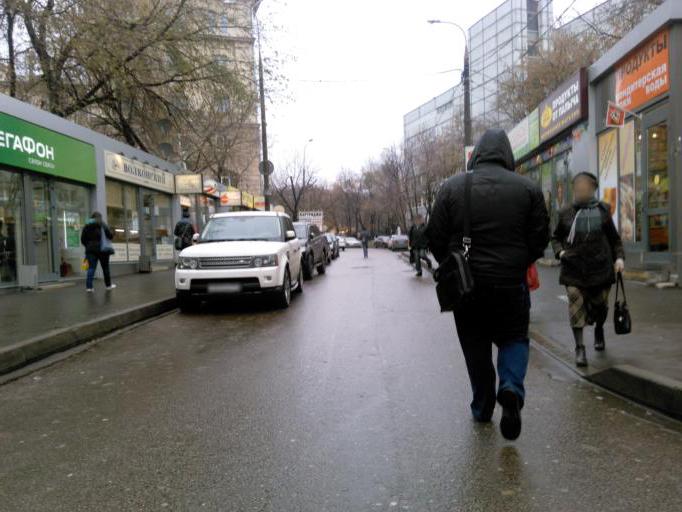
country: RU
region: Moscow
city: Novyye Cheremushki
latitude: 55.7086
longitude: 37.5877
